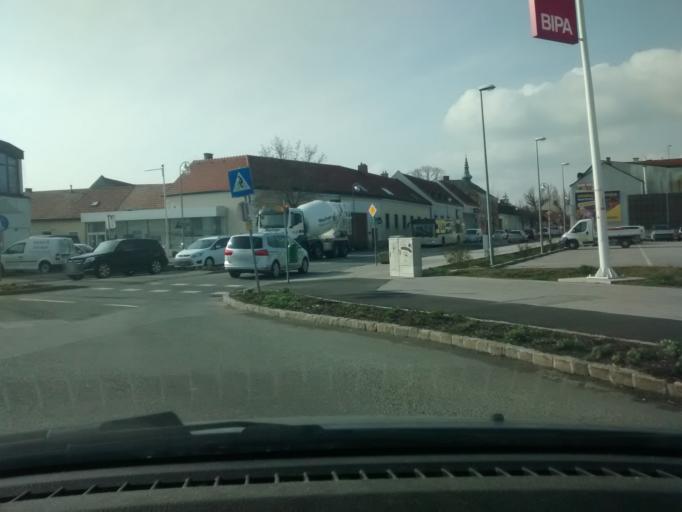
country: AT
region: Lower Austria
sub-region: Politischer Bezirk Baden
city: Traiskirchen
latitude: 48.0204
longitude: 16.2970
